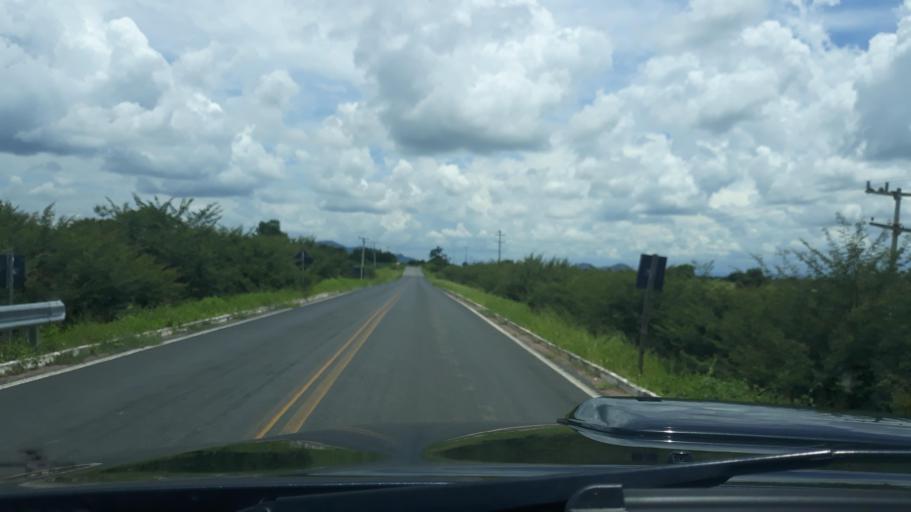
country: BR
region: Bahia
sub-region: Guanambi
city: Guanambi
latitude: -13.9553
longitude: -42.8547
